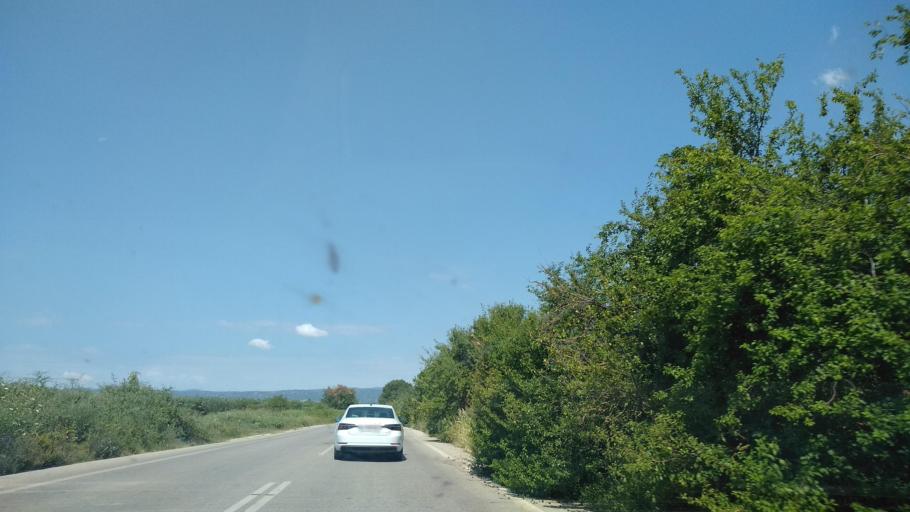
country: GR
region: Central Macedonia
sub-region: Nomos Thessalonikis
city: Nea Apollonia
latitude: 40.6292
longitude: 23.5283
